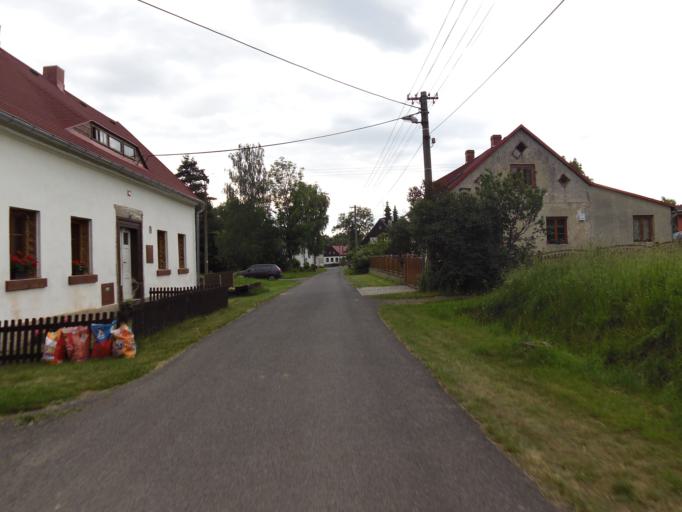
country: CZ
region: Ustecky
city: Varnsdorf
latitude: 50.8812
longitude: 14.6265
